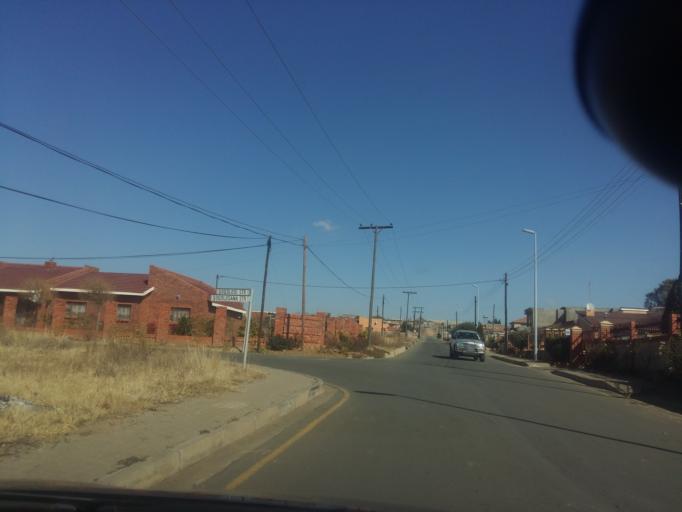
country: LS
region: Maseru
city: Maseru
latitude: -29.3460
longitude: 27.4535
